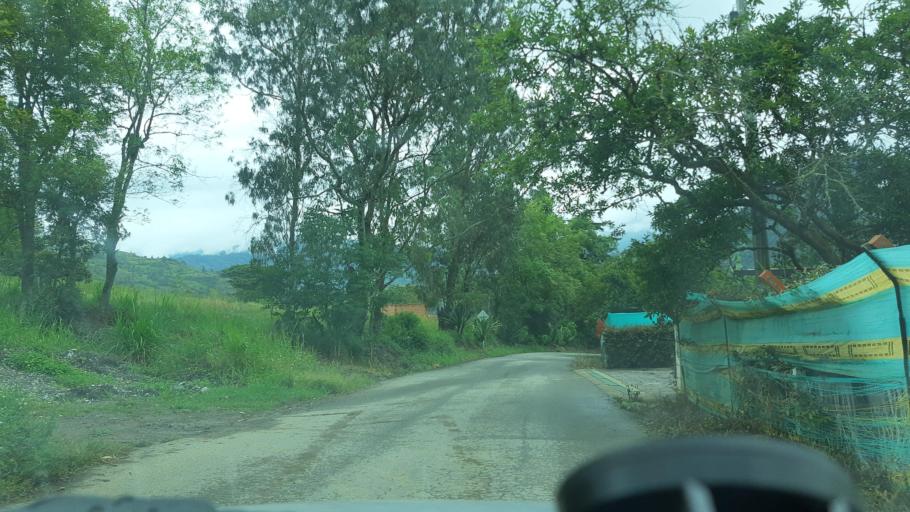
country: CO
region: Cundinamarca
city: Manta
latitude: 5.0446
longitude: -73.5108
